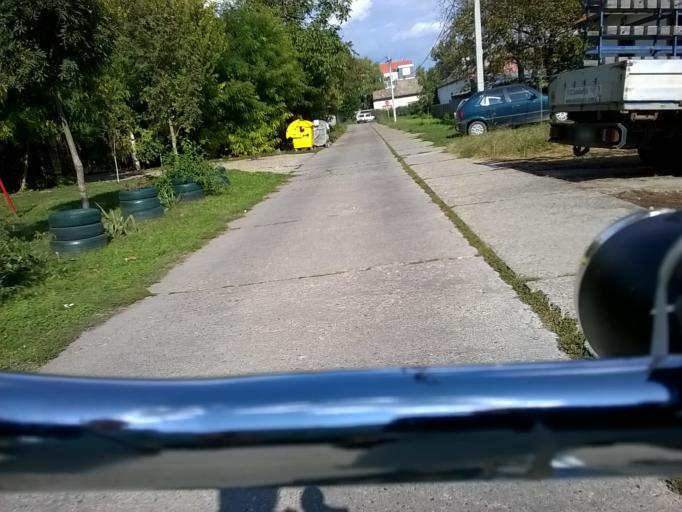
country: RS
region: Autonomna Pokrajina Vojvodina
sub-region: Juznobanatski Okrug
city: Pancevo
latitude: 44.8767
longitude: 20.6432
